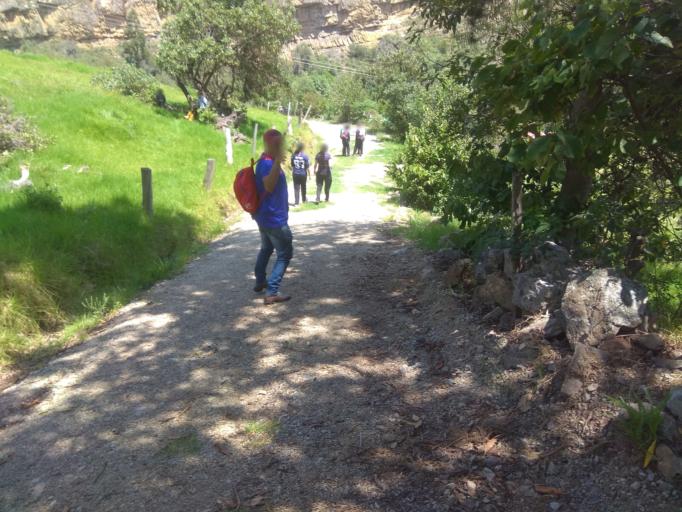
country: CO
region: Boyaca
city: Socha Viejo
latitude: 5.9999
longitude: -72.7117
